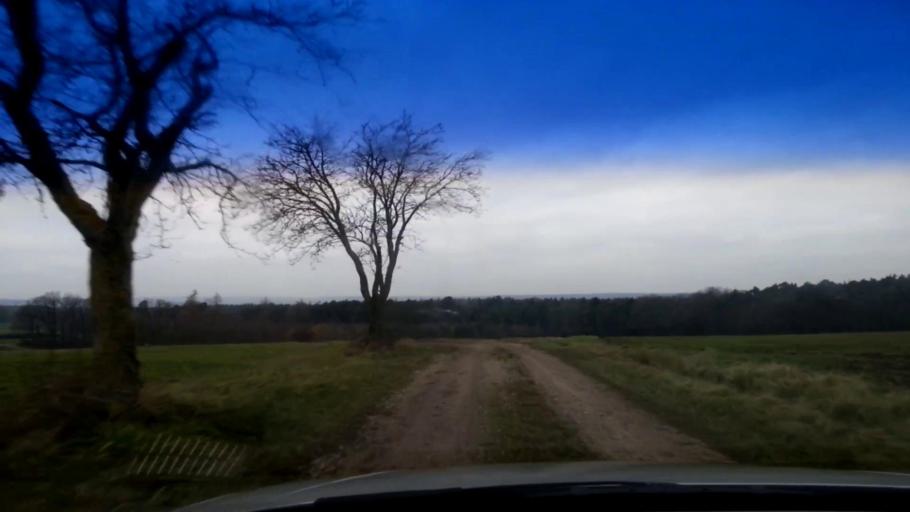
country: DE
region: Bavaria
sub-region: Upper Franconia
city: Pommersfelden
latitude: 49.8031
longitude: 10.7859
